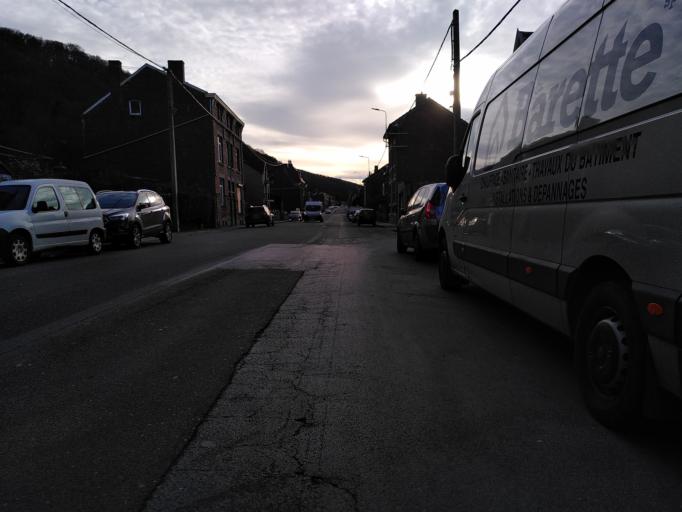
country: BE
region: Wallonia
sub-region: Province de Liege
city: Herstal
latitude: 50.6676
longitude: 5.6592
